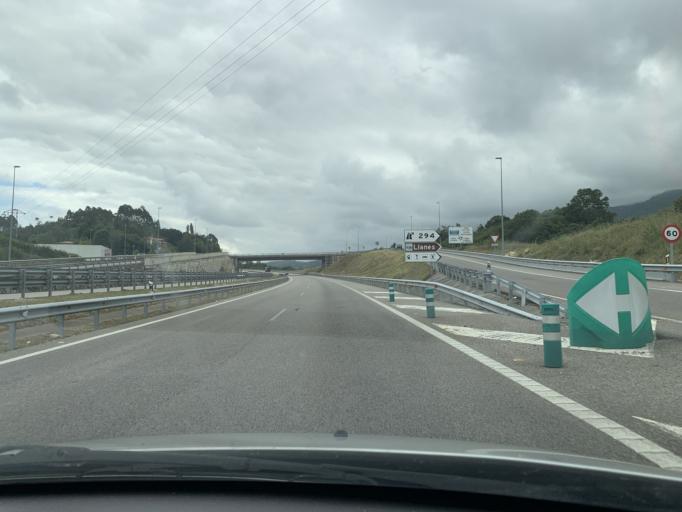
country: ES
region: Asturias
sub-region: Province of Asturias
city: Llanes
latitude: 43.4059
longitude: -4.7628
